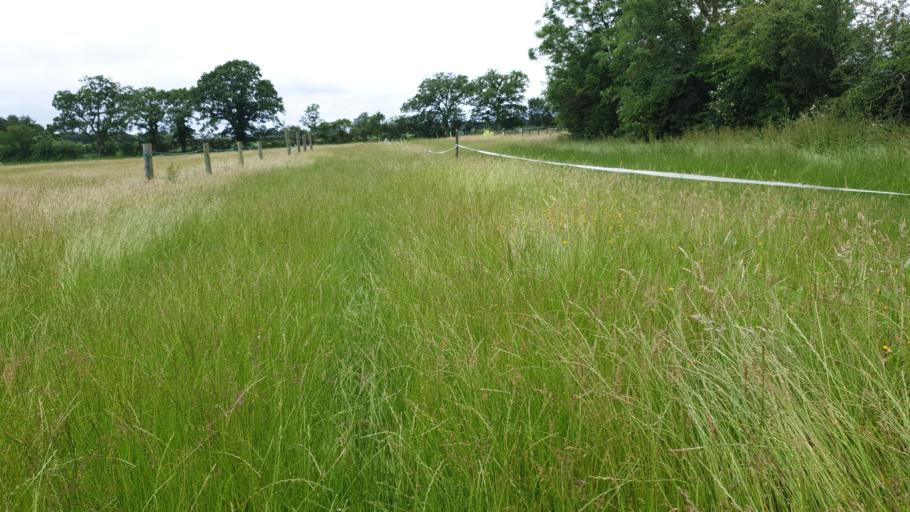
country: GB
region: England
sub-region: Essex
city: Great Bentley
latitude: 51.8853
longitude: 1.0644
